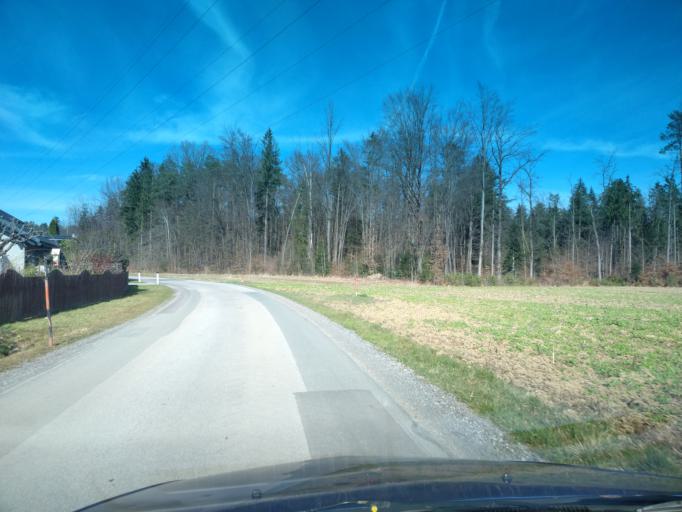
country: AT
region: Styria
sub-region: Politischer Bezirk Deutschlandsberg
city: Sankt Peter im Sulmtal
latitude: 46.7707
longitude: 15.2627
